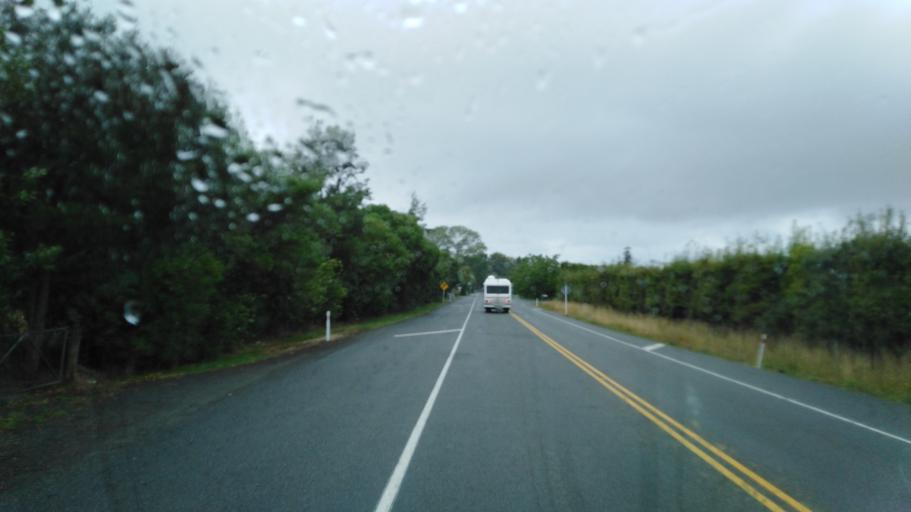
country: NZ
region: Marlborough
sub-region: Marlborough District
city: Blenheim
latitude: -41.4585
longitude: 173.9490
